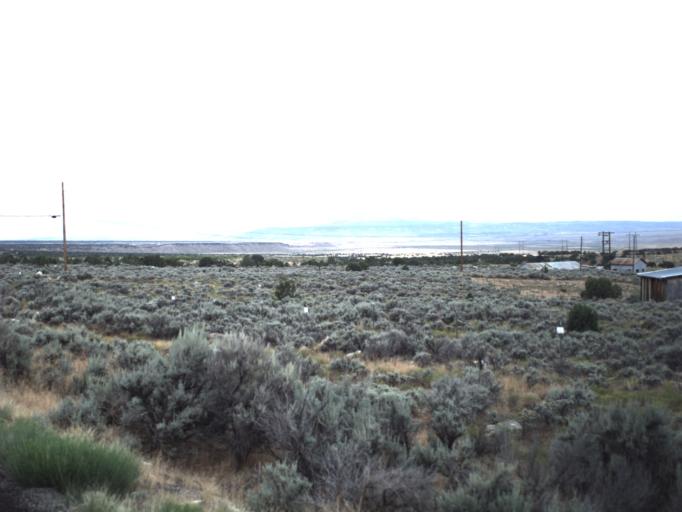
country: US
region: Utah
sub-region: Carbon County
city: East Carbon City
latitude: 39.5183
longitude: -110.3923
